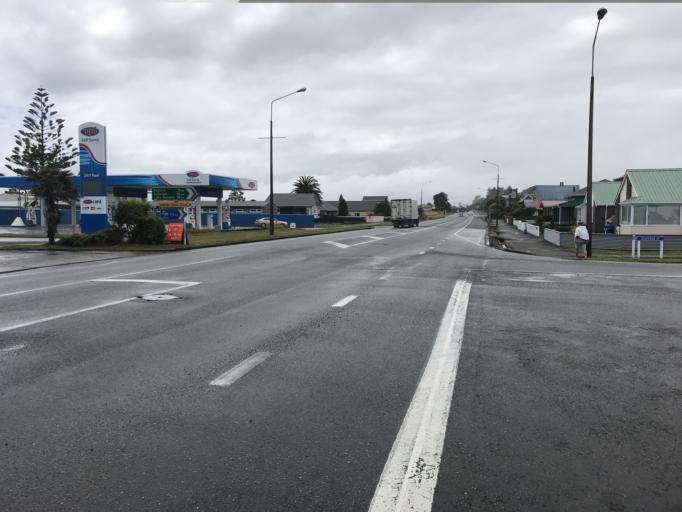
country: NZ
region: West Coast
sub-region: Westland District
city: Hokitika
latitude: -42.7175
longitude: 170.9665
